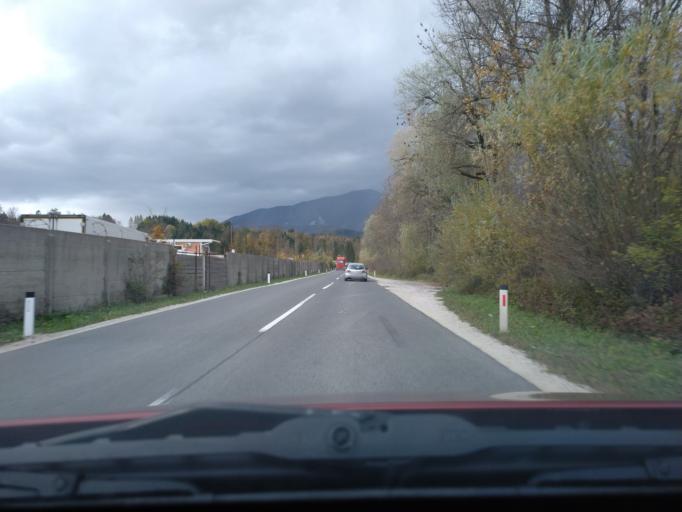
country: SI
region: Kamnik
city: Mekinje
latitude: 46.2362
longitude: 14.6081
